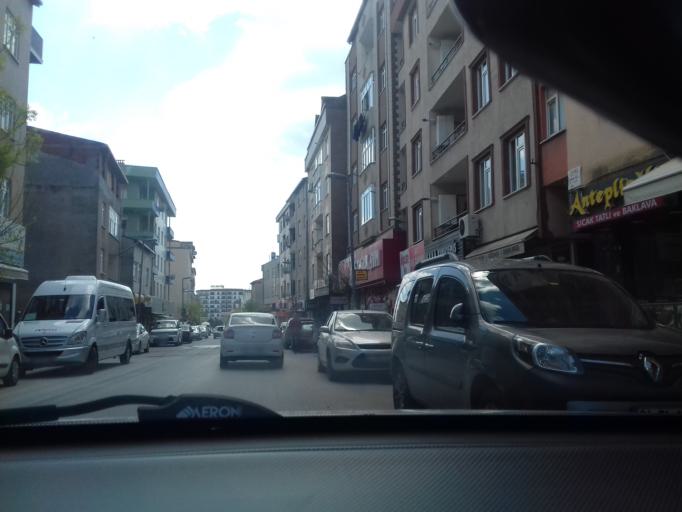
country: TR
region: Istanbul
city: Pendik
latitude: 40.8959
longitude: 29.2748
